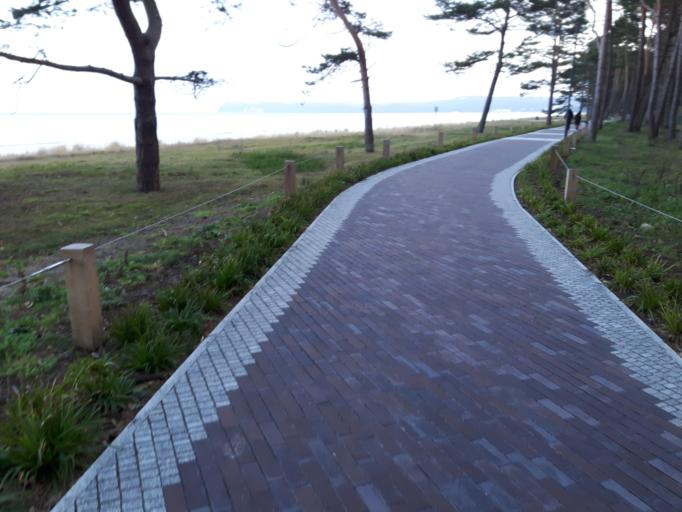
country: DE
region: Mecklenburg-Vorpommern
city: Ostseebad Binz
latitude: 54.4205
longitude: 13.5911
